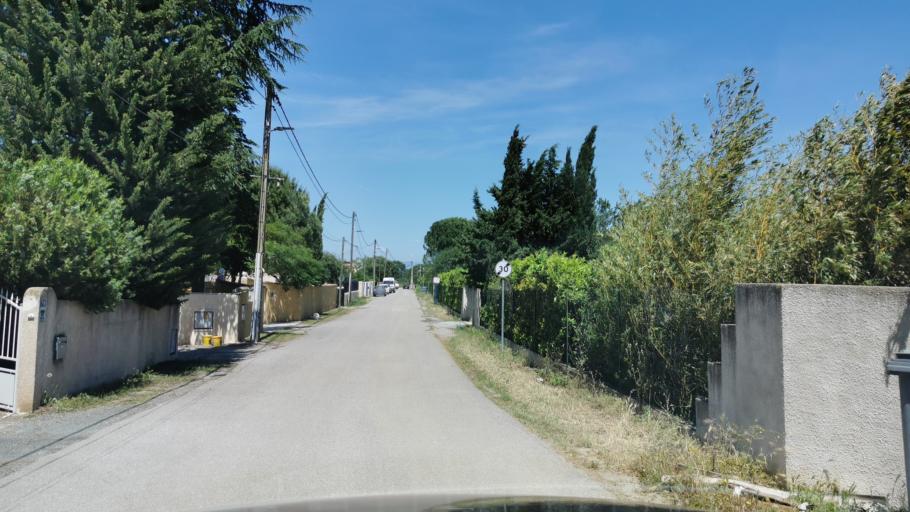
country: FR
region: Languedoc-Roussillon
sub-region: Departement de l'Aude
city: Coursan
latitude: 43.2677
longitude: 3.0230
